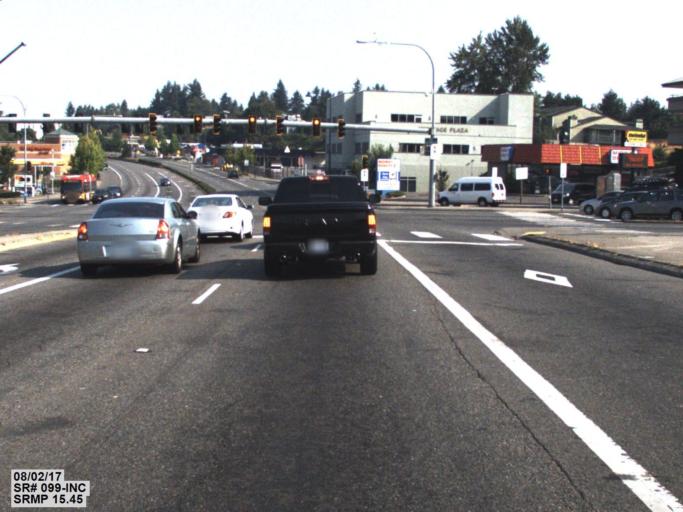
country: US
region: Washington
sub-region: King County
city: Des Moines
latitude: 47.3930
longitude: -122.2948
